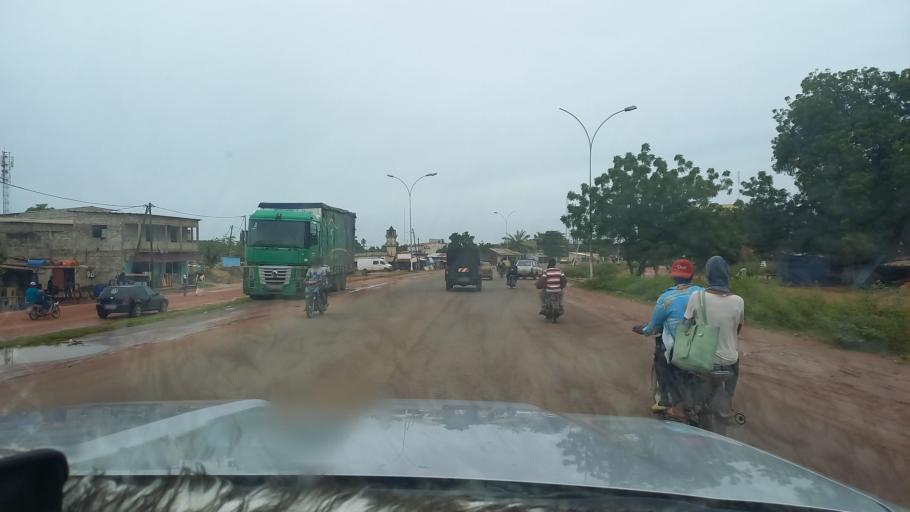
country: SN
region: Ziguinchor
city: Ziguinchor
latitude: 12.5713
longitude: -16.2714
